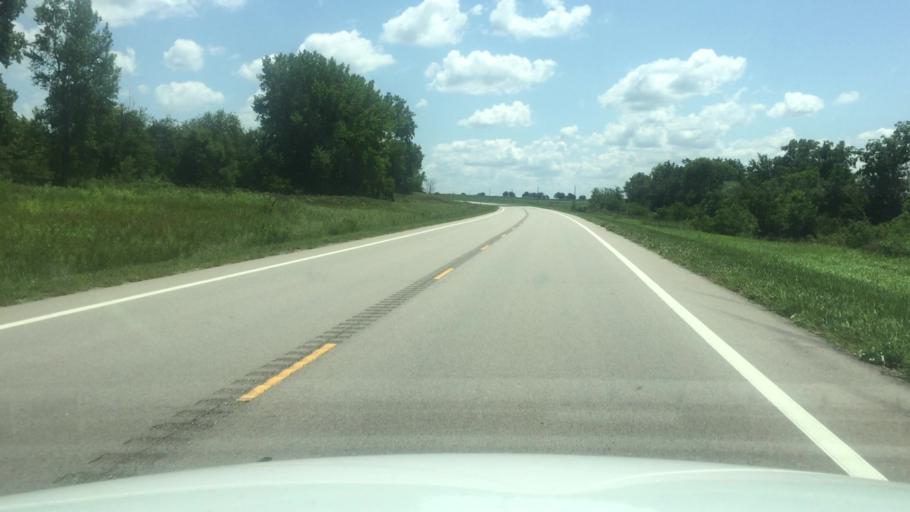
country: US
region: Kansas
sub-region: Brown County
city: Horton
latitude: 39.6187
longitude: -95.3489
